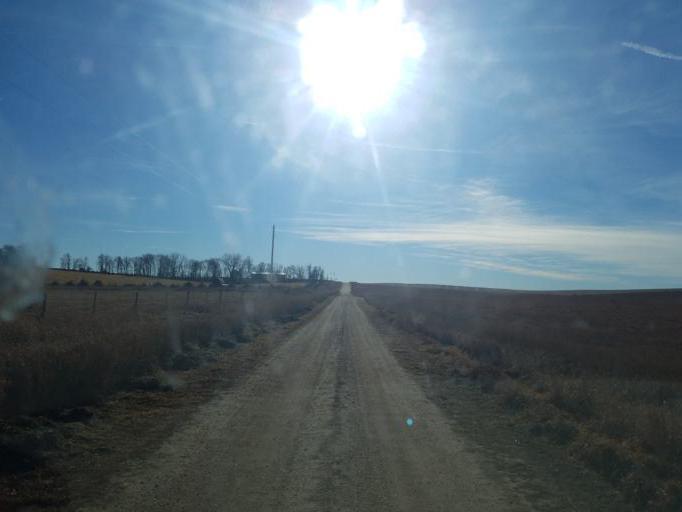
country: US
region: Nebraska
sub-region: Knox County
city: Center
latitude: 42.6526
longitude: -97.7991
